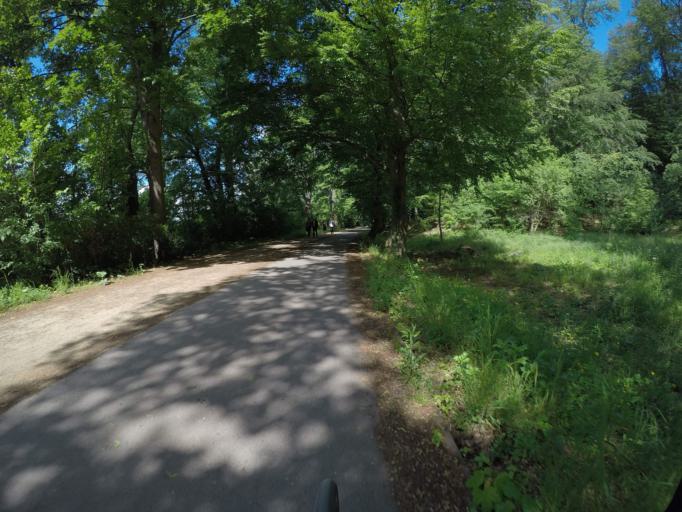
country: DE
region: Brandenburg
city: Potsdam
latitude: 52.4178
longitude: 13.0955
